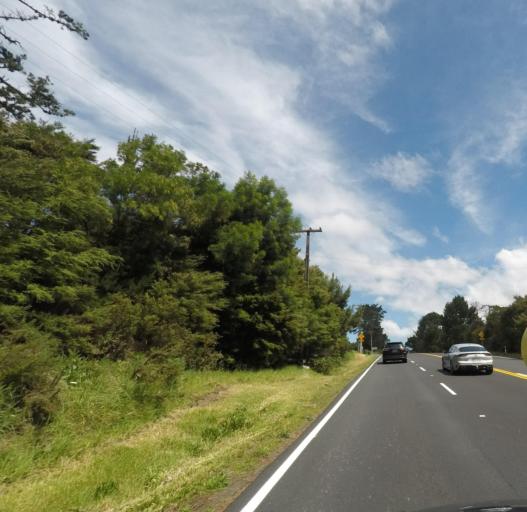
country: NZ
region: Auckland
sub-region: Auckland
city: Rothesay Bay
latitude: -36.6878
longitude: 174.7060
